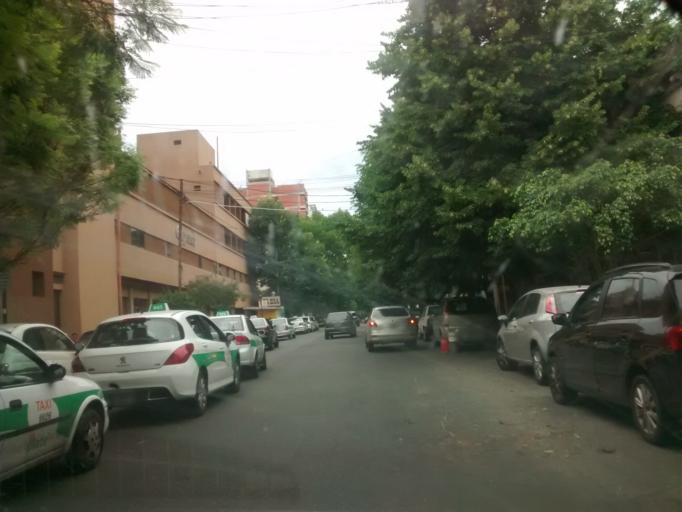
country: AR
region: Buenos Aires
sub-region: Partido de La Plata
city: La Plata
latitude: -34.9167
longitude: -57.9391
